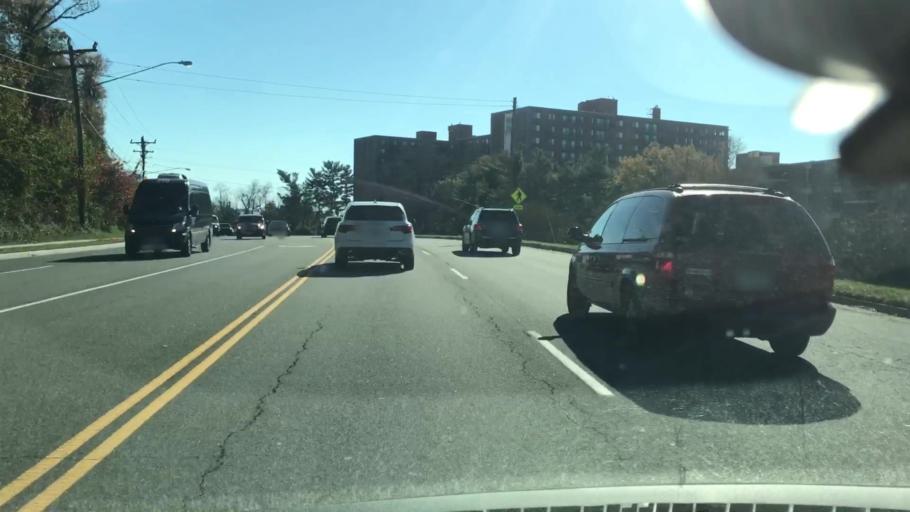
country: US
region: Virginia
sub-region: Fairfax County
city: Seven Corners
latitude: 38.8601
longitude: -77.1465
